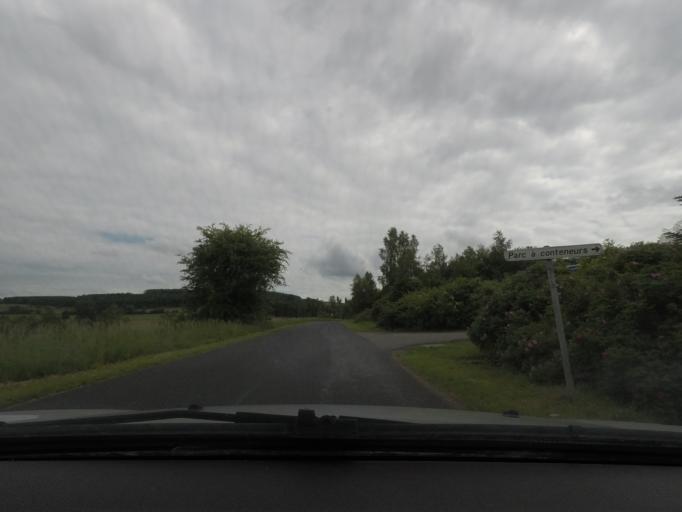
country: BE
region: Wallonia
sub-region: Province du Luxembourg
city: Leglise
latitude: 49.8104
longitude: 5.5412
